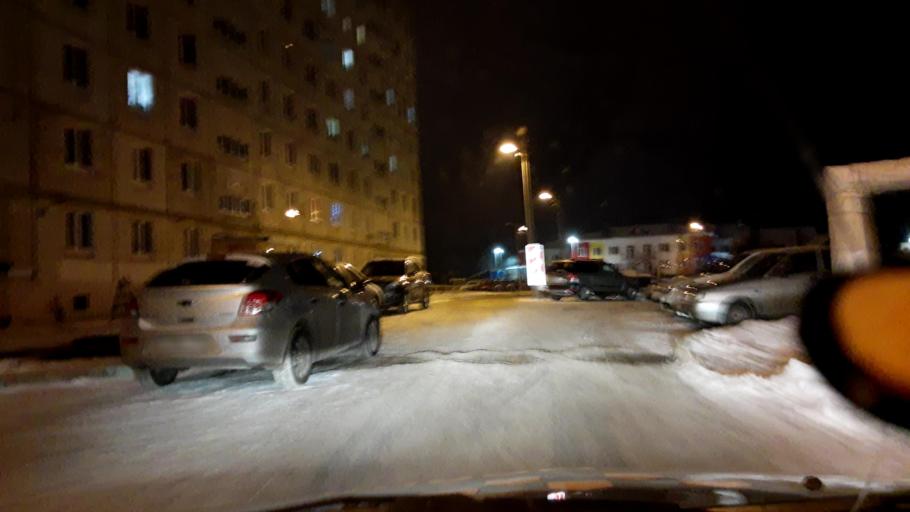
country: RU
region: Bashkortostan
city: Avdon
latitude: 54.7099
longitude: 55.8143
